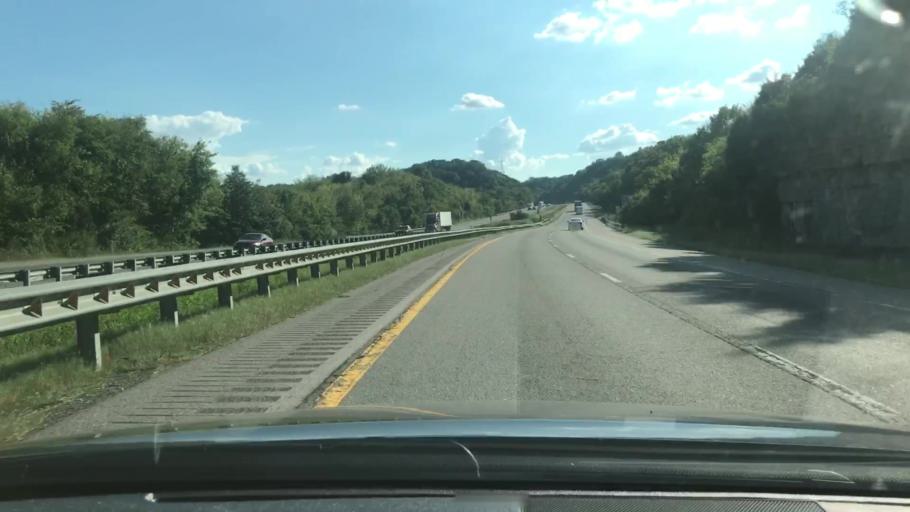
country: US
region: Tennessee
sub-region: Sumner County
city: Millersville
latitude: 36.3688
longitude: -86.7145
